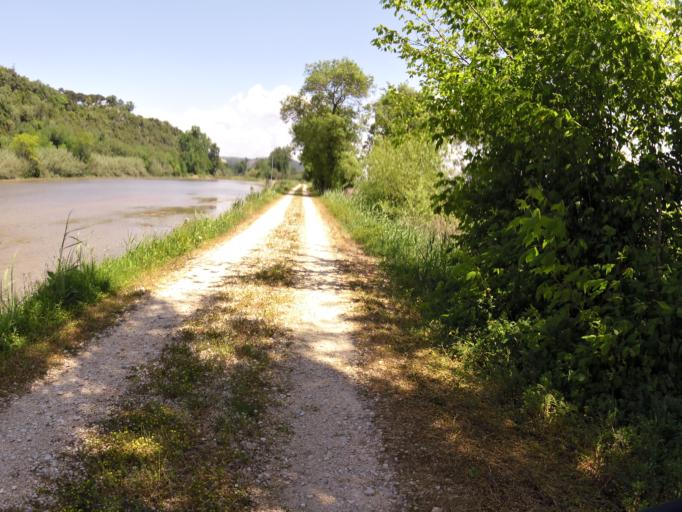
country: PT
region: Coimbra
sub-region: Montemor-O-Velho
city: Montemor-o-Velho
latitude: 40.1714
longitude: -8.7031
